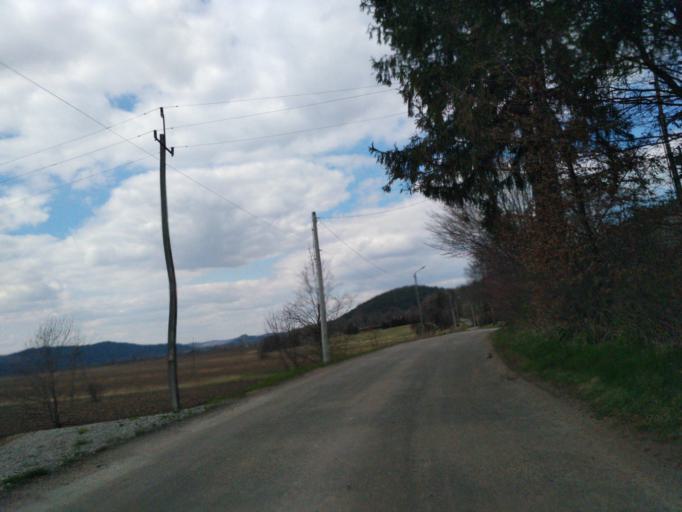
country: PL
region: Subcarpathian Voivodeship
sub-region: Powiat sanocki
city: Tyrawa Woloska
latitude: 49.6655
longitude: 22.2897
